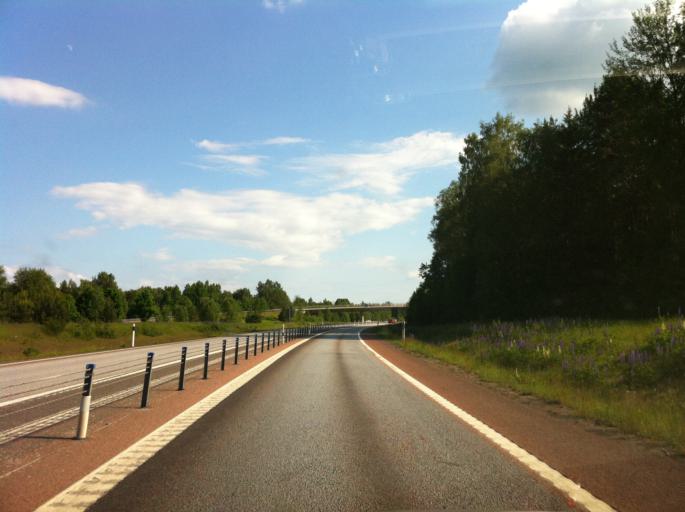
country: SE
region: Vaermland
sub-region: Karlstads Kommun
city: Karlstad
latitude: 59.4321
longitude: 13.4046
